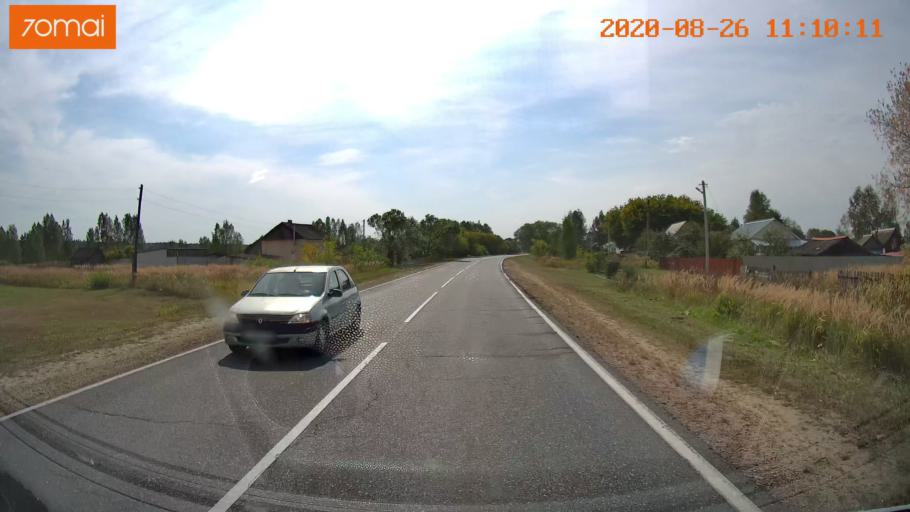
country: RU
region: Rjazan
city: Izhevskoye
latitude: 54.4810
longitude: 41.1263
